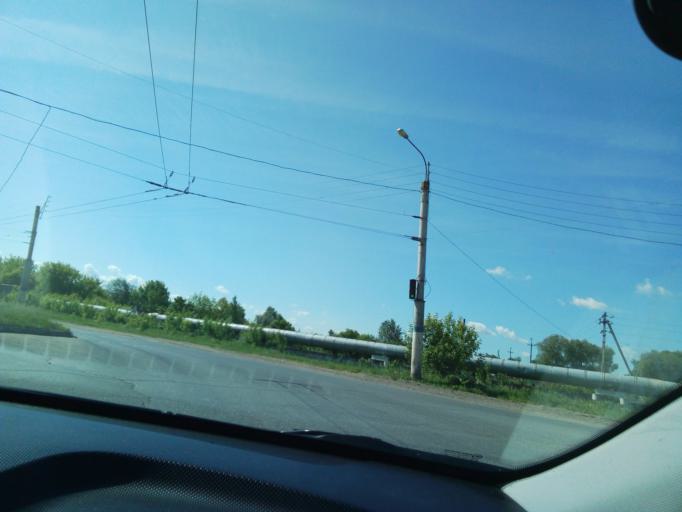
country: RU
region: Chuvashia
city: Novocheboksarsk
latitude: 56.0947
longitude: 47.4944
